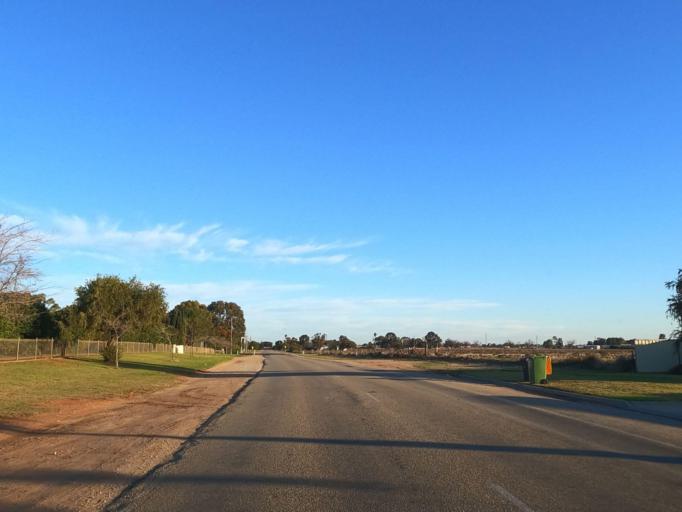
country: AU
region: Victoria
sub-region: Swan Hill
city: Swan Hill
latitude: -35.3543
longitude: 143.5528
